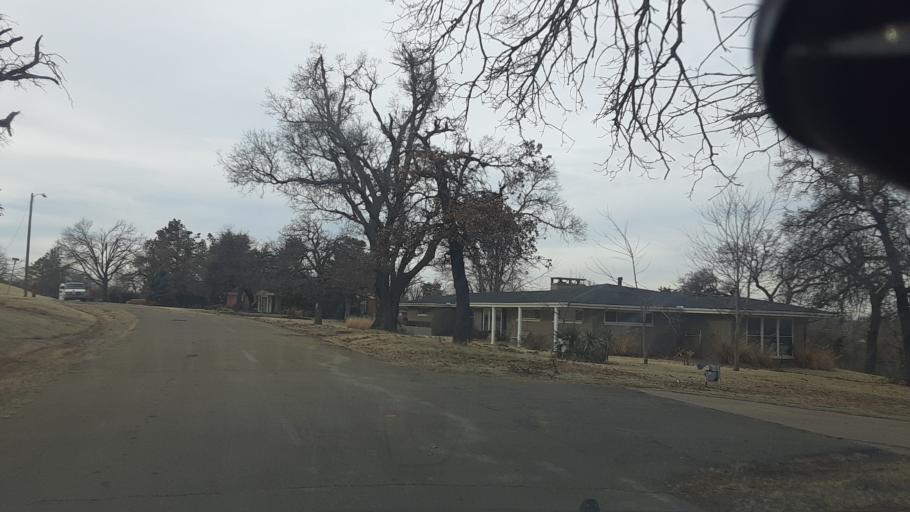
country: US
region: Oklahoma
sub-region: Logan County
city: Guthrie
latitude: 35.8842
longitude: -97.4132
